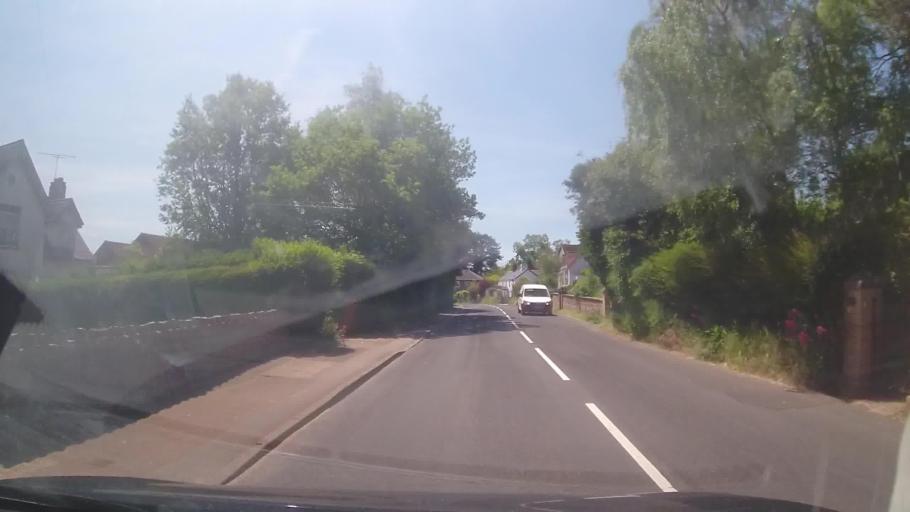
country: GB
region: Wales
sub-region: Monmouthshire
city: Monmouth
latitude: 51.8269
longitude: -2.7125
